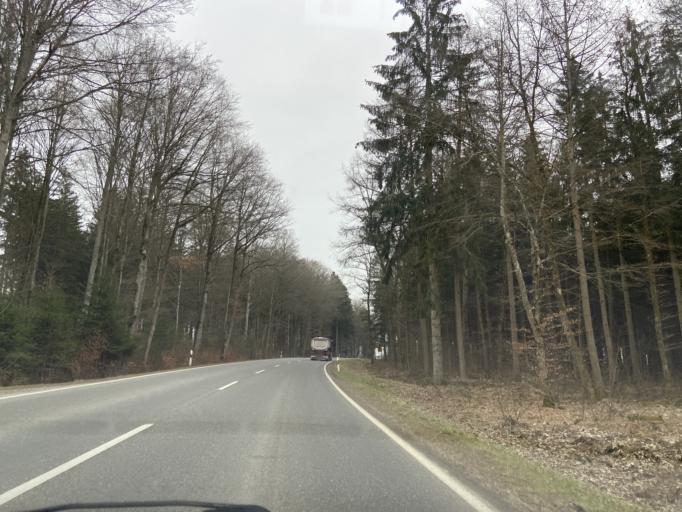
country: DE
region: Baden-Wuerttemberg
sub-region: Tuebingen Region
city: Ennetach
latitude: 47.9952
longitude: 9.3087
